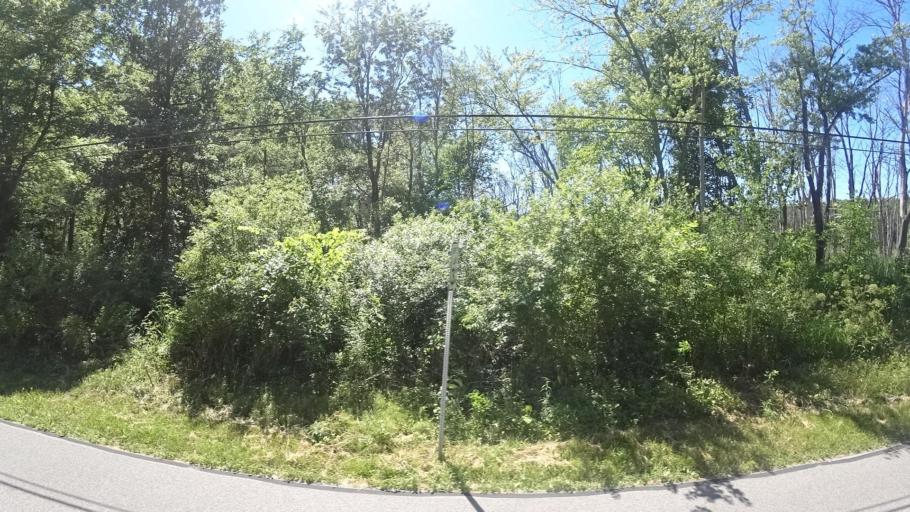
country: US
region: Indiana
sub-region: Porter County
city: Porter
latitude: 41.6488
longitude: -87.0674
